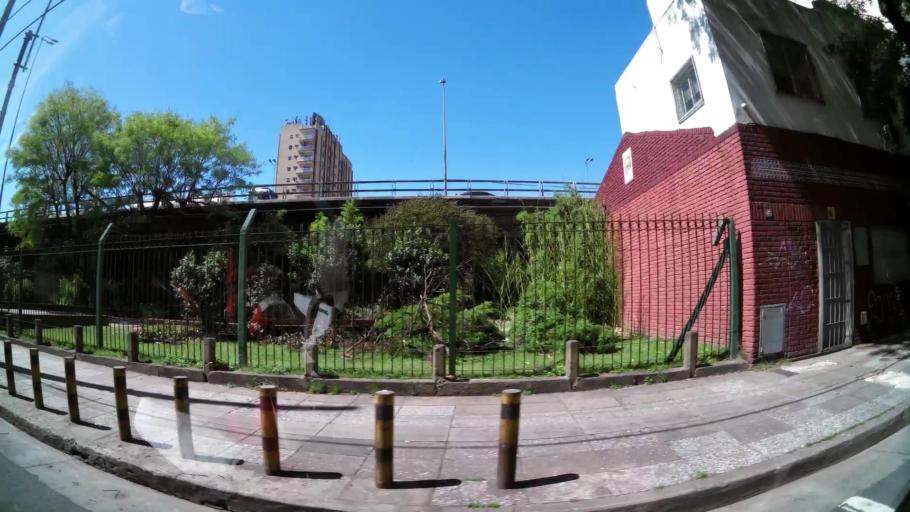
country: AR
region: Buenos Aires F.D.
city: Buenos Aires
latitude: -34.6244
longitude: -58.3973
